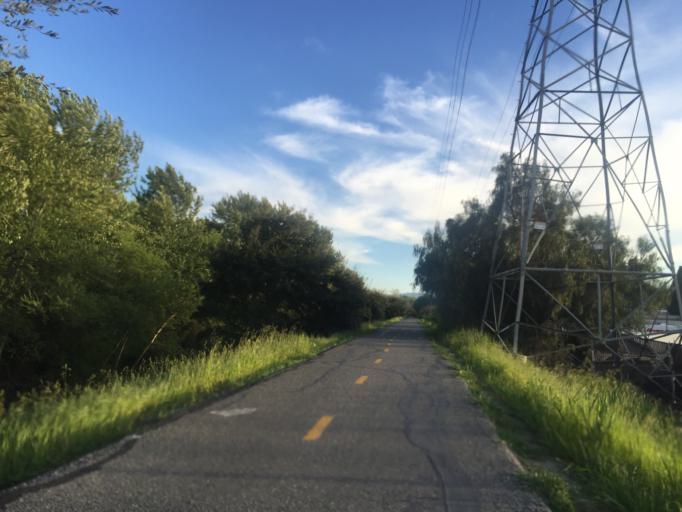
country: US
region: California
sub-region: Santa Clara County
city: Mountain View
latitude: 37.4157
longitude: -122.0689
